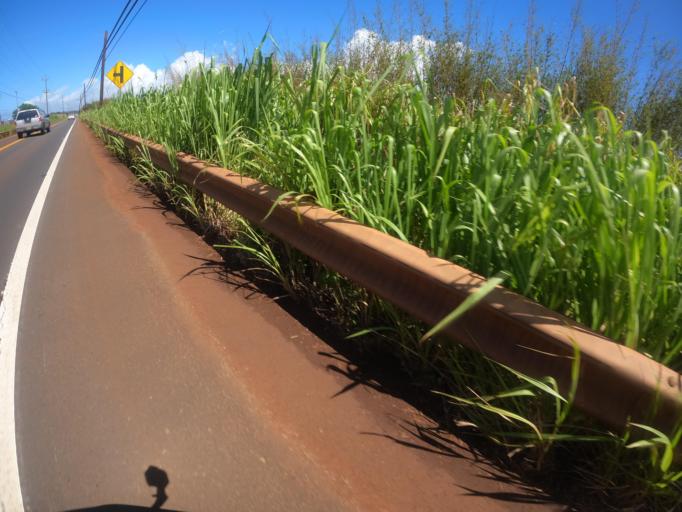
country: US
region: Hawaii
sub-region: Honolulu County
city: Schofield Barracks
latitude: 21.4620
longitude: -158.0563
